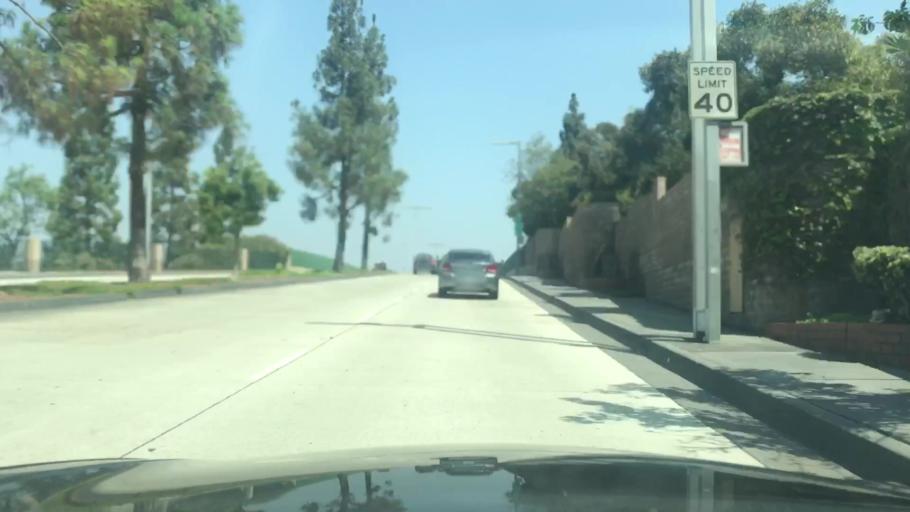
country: US
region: California
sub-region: Los Angeles County
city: Cerritos
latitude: 33.8685
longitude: -118.0550
